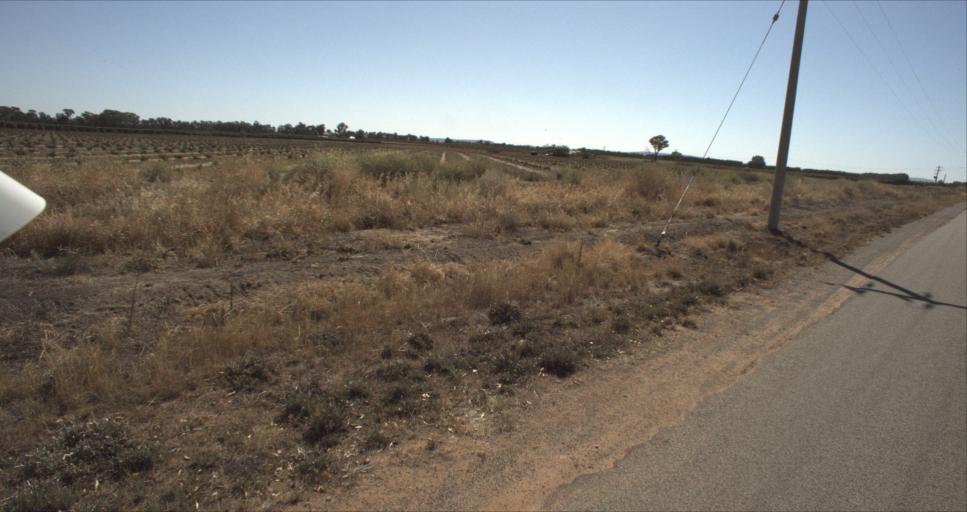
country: AU
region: New South Wales
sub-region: Leeton
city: Leeton
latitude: -34.5392
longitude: 146.3363
